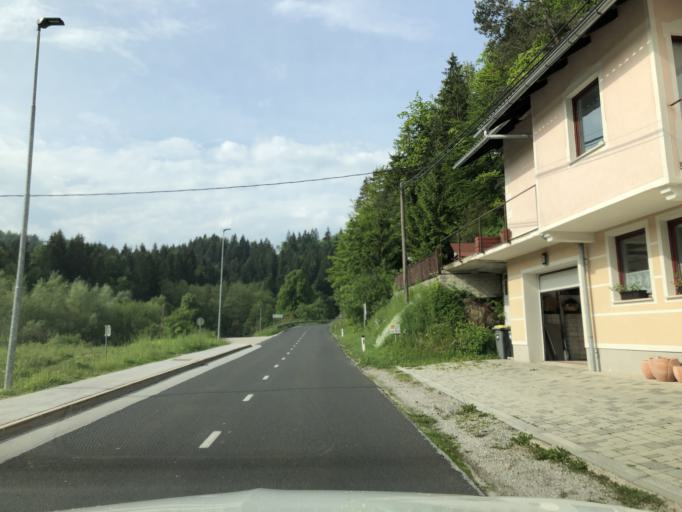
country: SI
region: Velike Lasce
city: Velike Lasce
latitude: 45.8275
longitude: 14.6363
